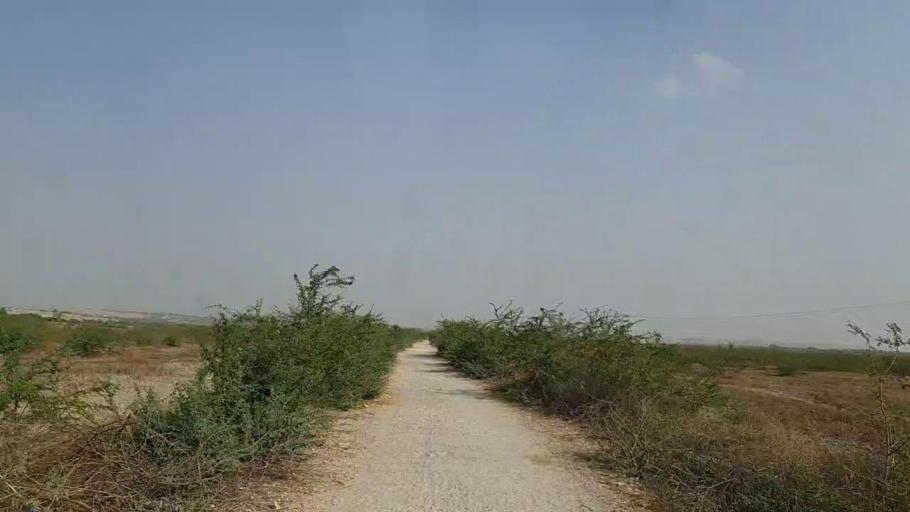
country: PK
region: Sindh
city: Naukot
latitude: 24.6660
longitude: 69.2773
